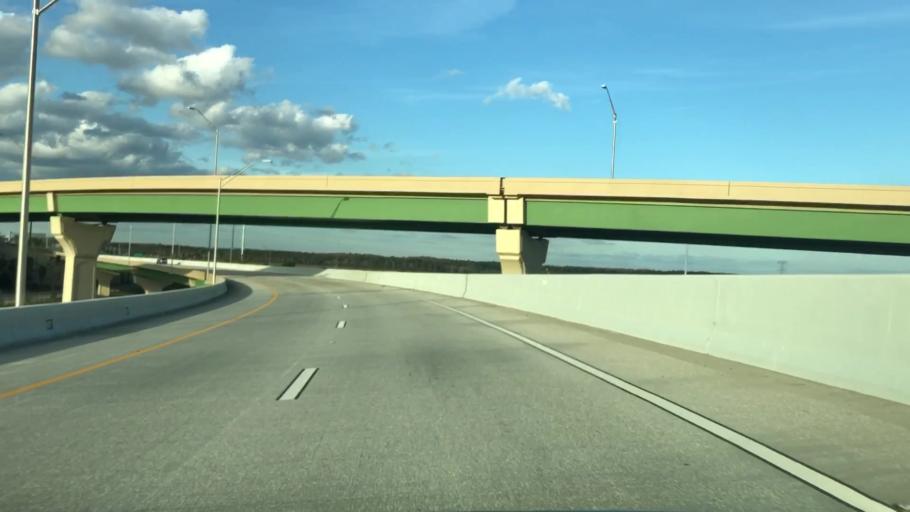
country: US
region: Florida
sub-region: Osceola County
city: Buenaventura Lakes
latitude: 28.3694
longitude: -81.3103
